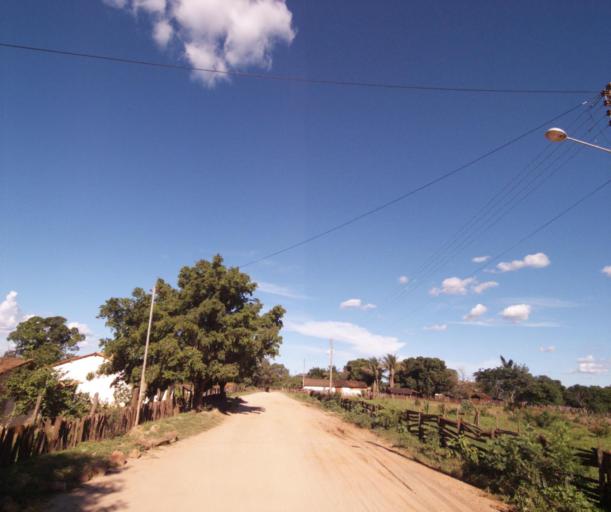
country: BR
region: Bahia
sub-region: Carinhanha
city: Carinhanha
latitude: -14.2748
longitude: -44.5116
